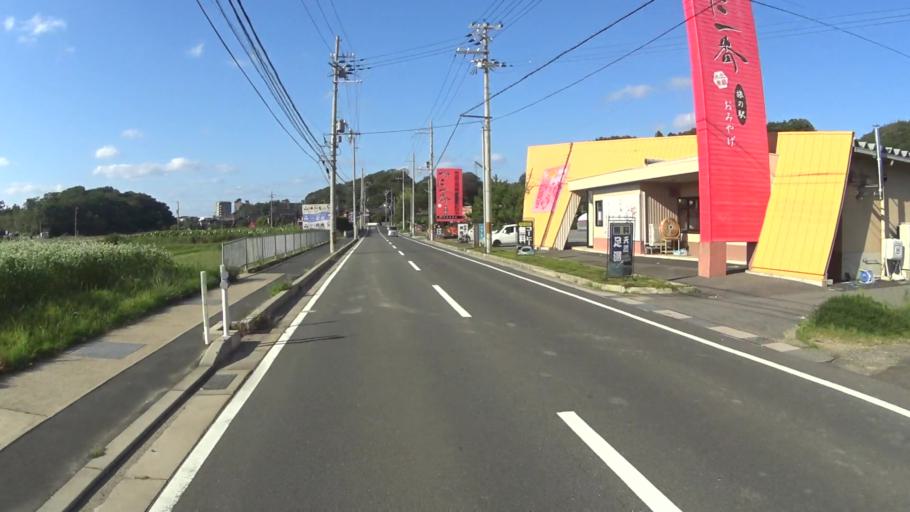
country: JP
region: Hyogo
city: Toyooka
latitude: 35.6518
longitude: 134.9699
